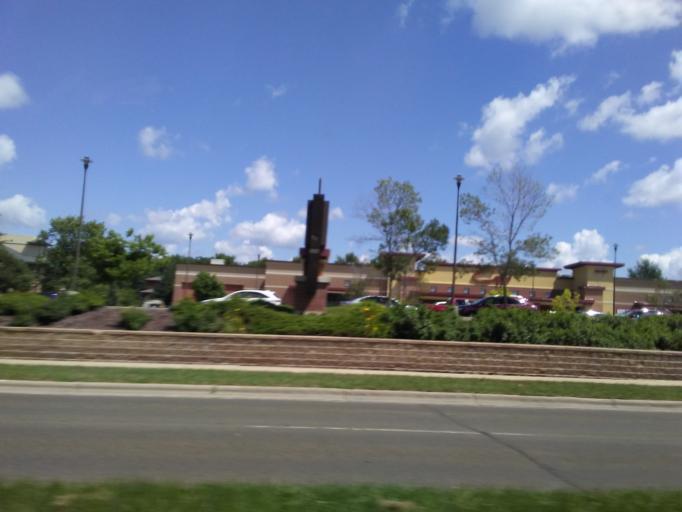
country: US
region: Wisconsin
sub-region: Dane County
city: Middleton
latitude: 43.1070
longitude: -89.4992
